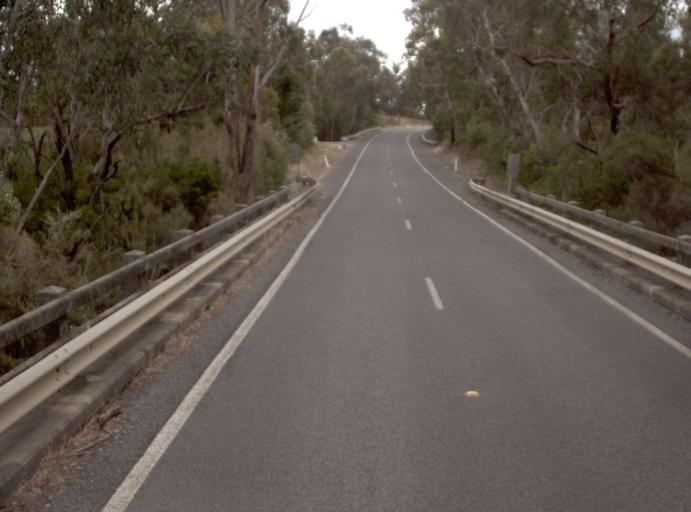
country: AU
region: Victoria
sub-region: Wellington
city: Sale
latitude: -38.3283
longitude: 147.0180
